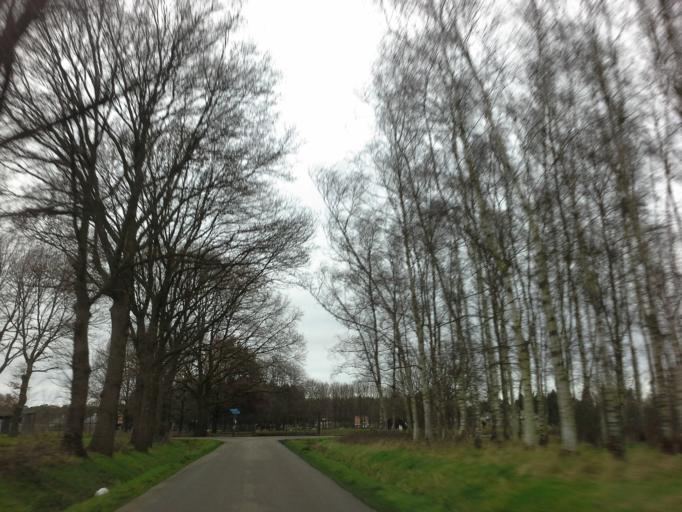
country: BE
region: Flanders
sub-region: Provincie Antwerpen
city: Meerhout
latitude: 51.1209
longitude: 5.0655
